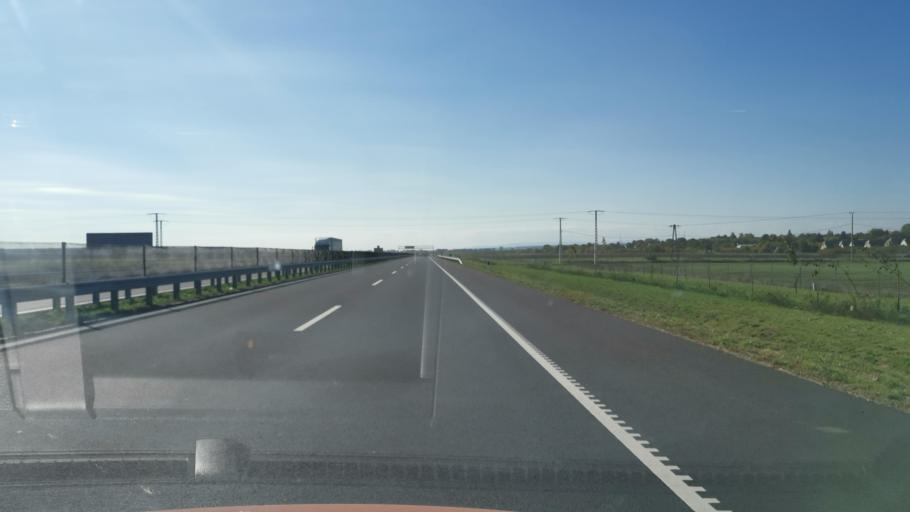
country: HU
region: Borsod-Abauj-Zemplen
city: Encs
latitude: 48.3229
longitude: 21.0963
